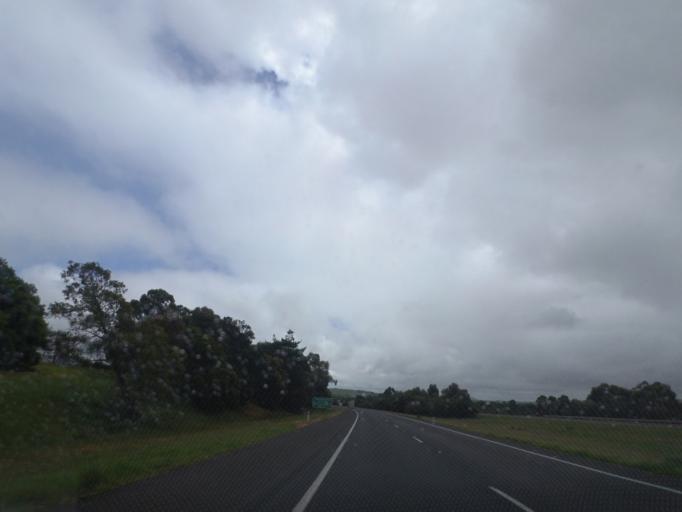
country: AU
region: Victoria
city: Black Hill
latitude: -37.5273
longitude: 143.8688
